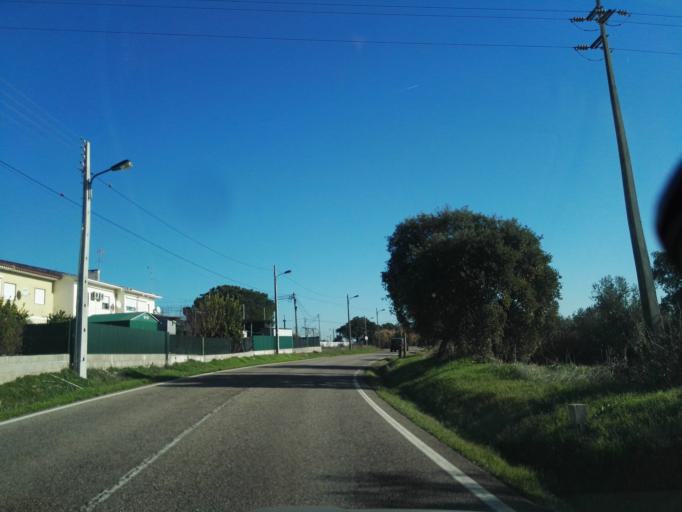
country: PT
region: Santarem
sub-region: Constancia
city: Constancia
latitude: 39.4823
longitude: -8.3036
